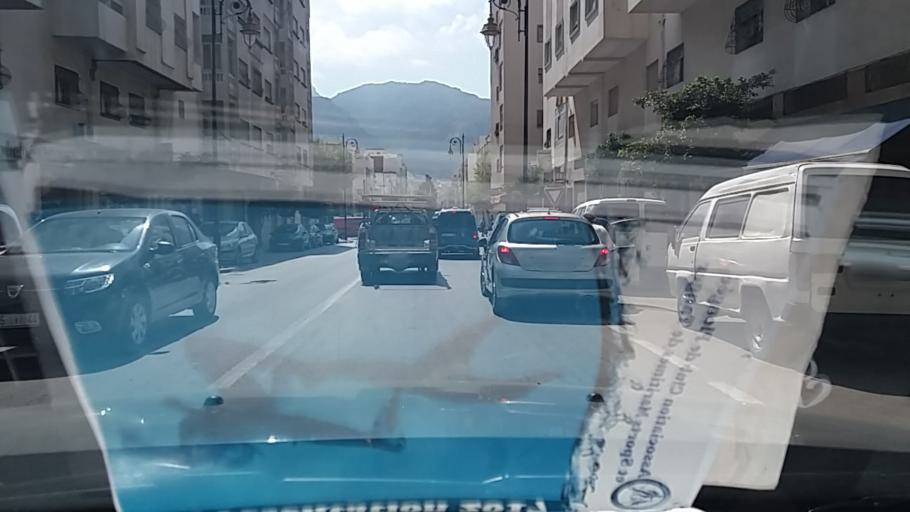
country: MA
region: Tanger-Tetouan
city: Tetouan
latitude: 35.5663
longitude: -5.3576
